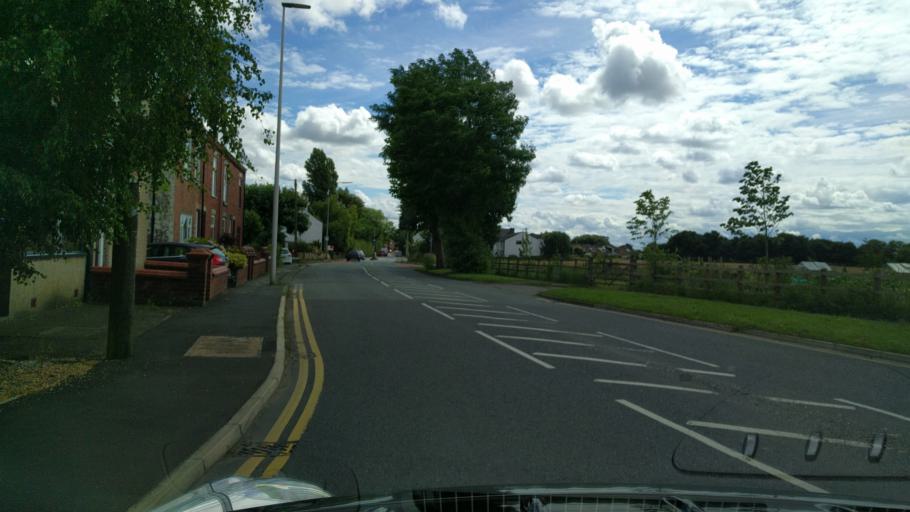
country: GB
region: England
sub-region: Borough of Wigan
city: Leigh
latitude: 53.4750
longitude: -2.4963
